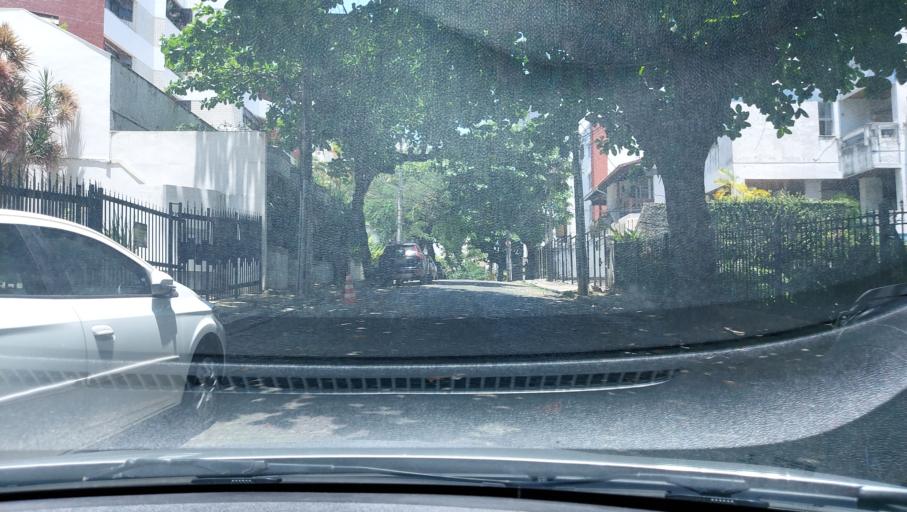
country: BR
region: Bahia
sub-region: Salvador
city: Salvador
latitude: -12.9916
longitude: -38.4525
